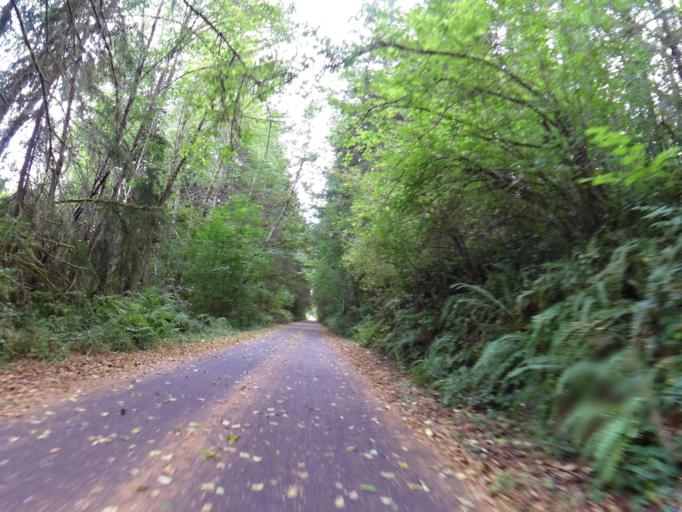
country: US
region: Washington
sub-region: Thurston County
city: Lacey
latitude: 46.9707
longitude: -122.8128
